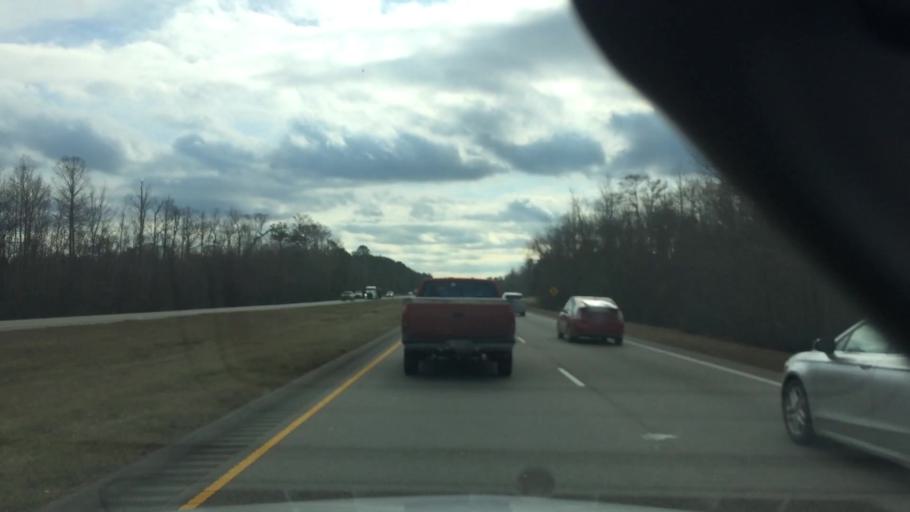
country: US
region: North Carolina
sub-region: Brunswick County
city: Leland
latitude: 34.1621
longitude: -78.0906
